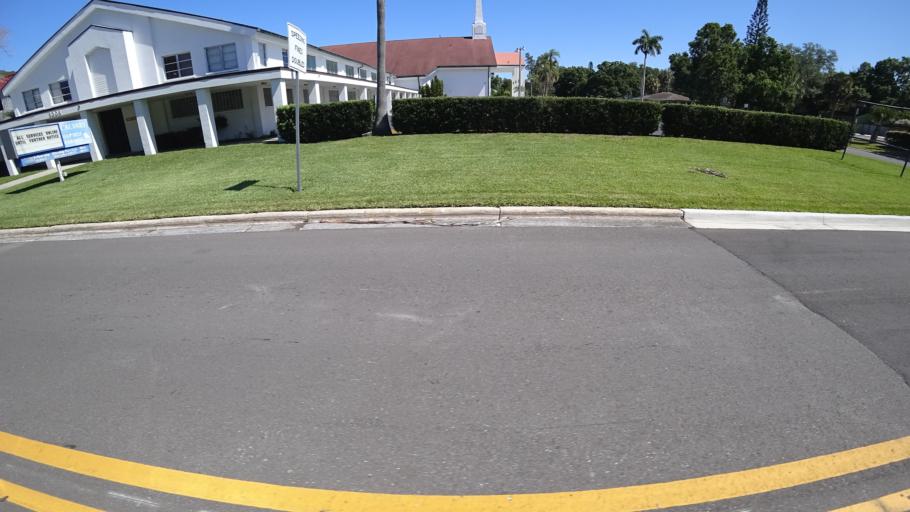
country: US
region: Florida
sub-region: Manatee County
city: Bradenton
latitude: 27.4920
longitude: -82.5920
